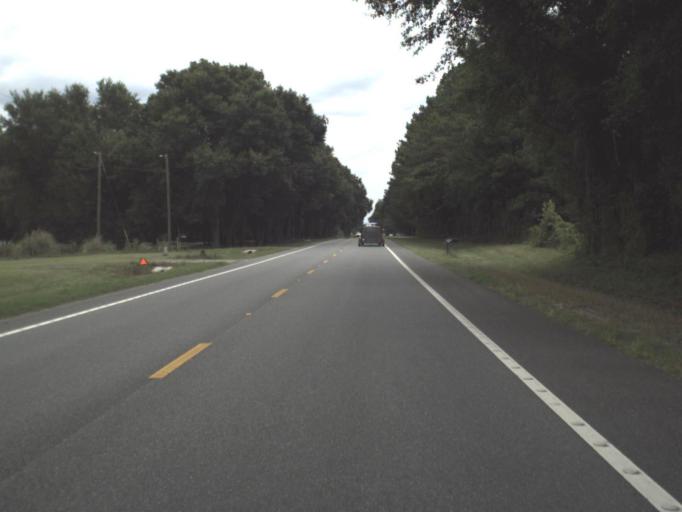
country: US
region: Florida
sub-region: Suwannee County
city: Wellborn
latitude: 29.9922
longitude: -82.8678
